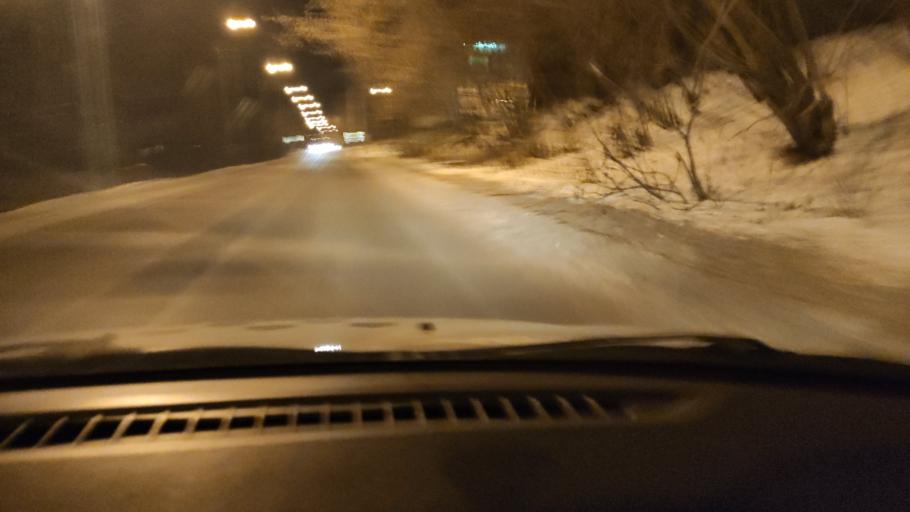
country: RU
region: Perm
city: Perm
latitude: 58.1004
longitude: 56.3056
